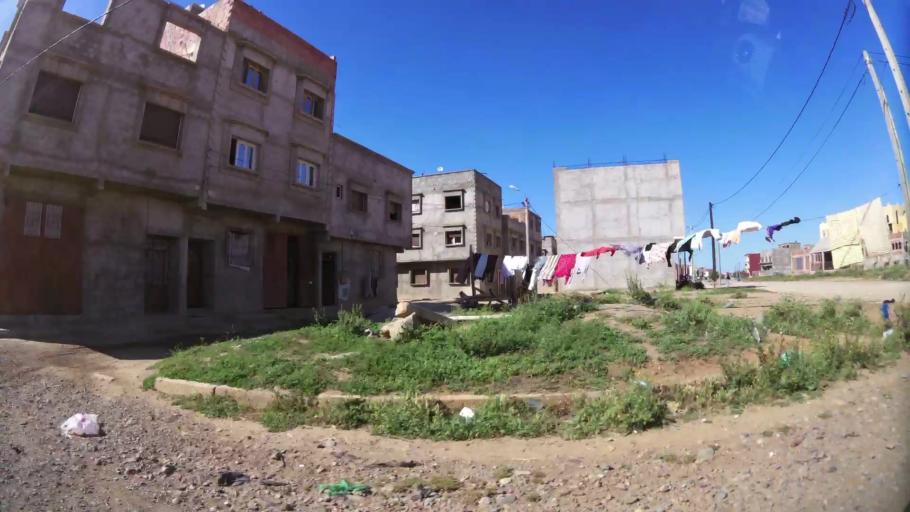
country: MA
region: Oriental
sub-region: Berkane-Taourirt
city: Berkane
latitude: 34.9389
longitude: -2.3414
